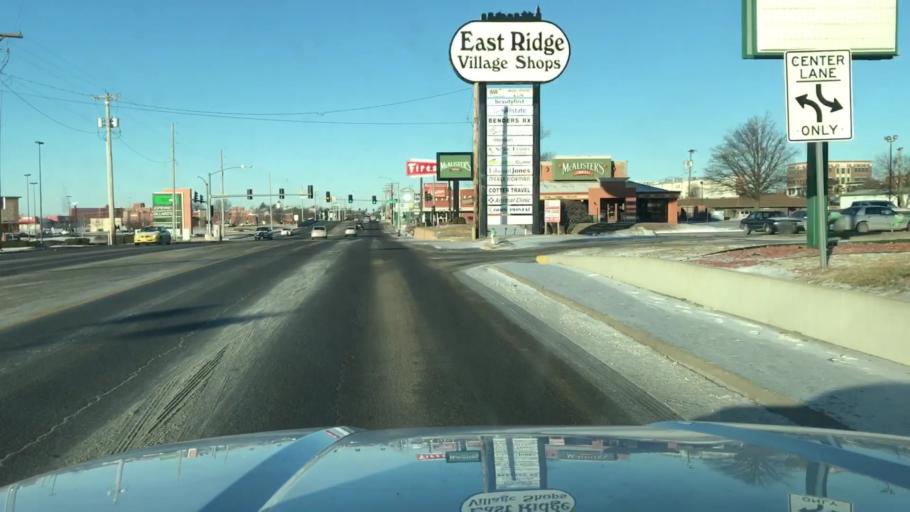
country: US
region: Missouri
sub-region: Buchanan County
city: Saint Joseph
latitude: 39.7771
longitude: -94.7986
